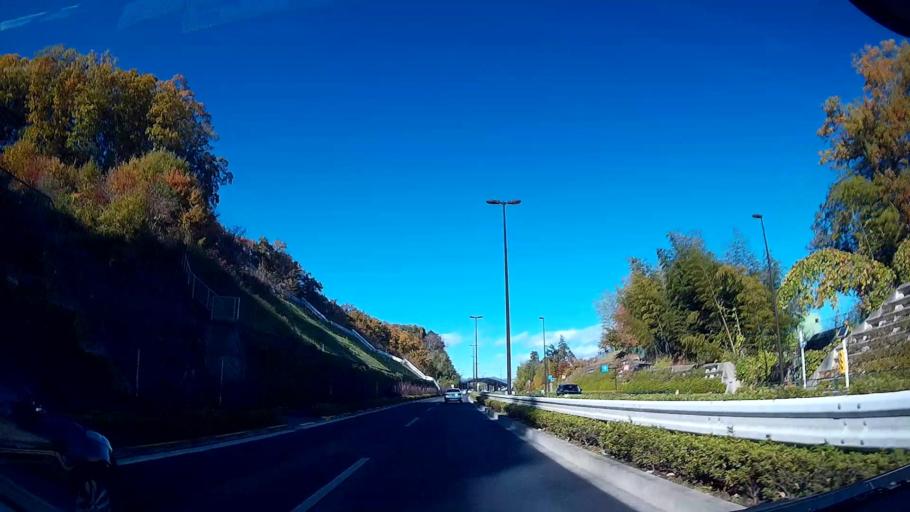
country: JP
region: Tokyo
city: Fussa
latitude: 35.6999
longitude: 139.3123
